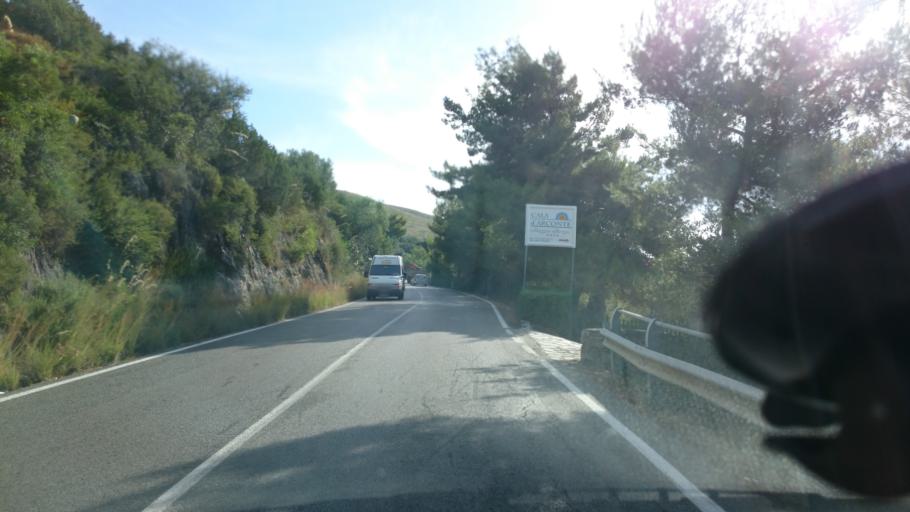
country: IT
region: Campania
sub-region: Provincia di Salerno
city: Marina di Camerota
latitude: 40.0065
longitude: 15.3460
